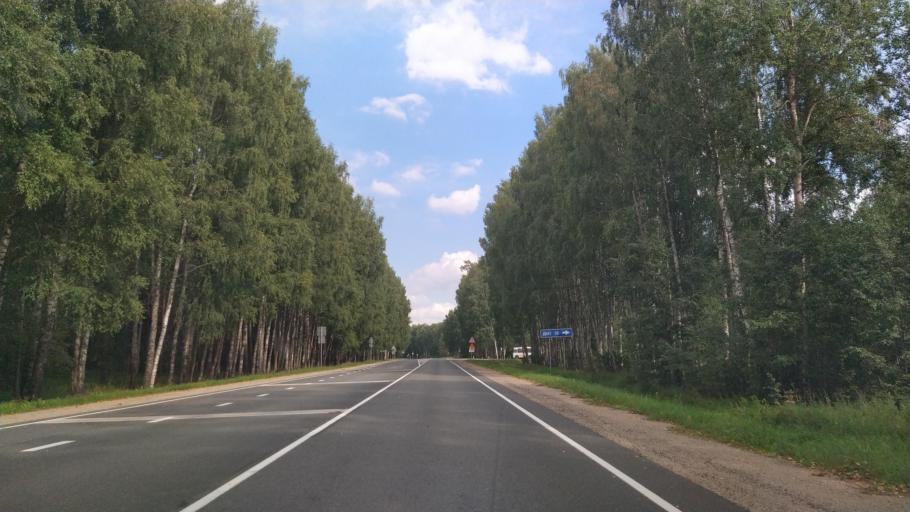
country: RU
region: Pskov
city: Dno
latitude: 57.9829
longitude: 29.7837
